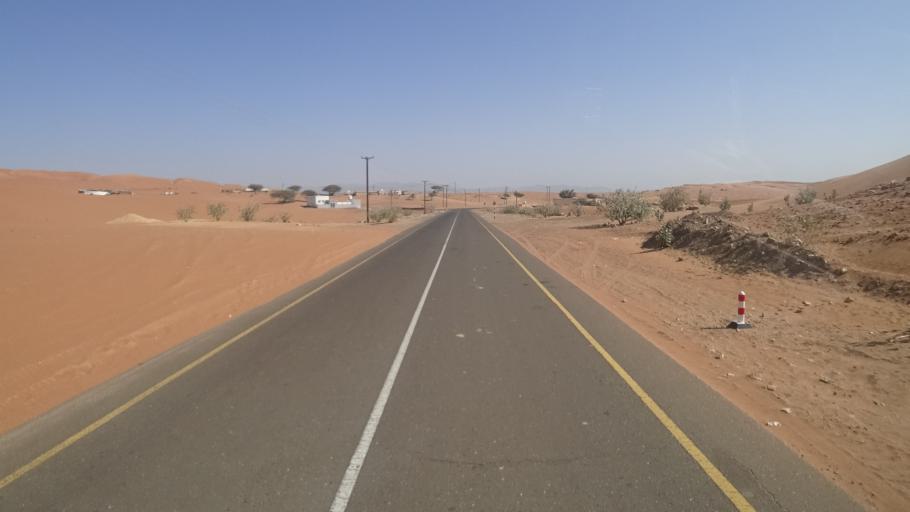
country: OM
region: Ash Sharqiyah
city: Al Qabil
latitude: 22.4835
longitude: 58.7120
